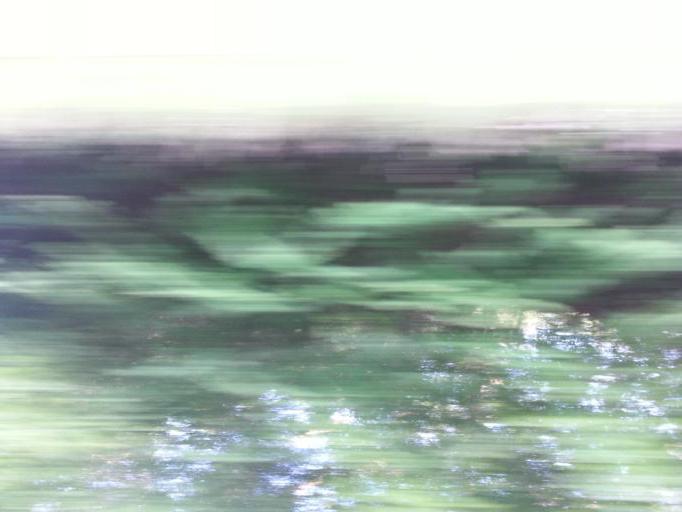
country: US
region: Georgia
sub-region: Towns County
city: Hiawassee
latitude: 34.8222
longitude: -83.8243
